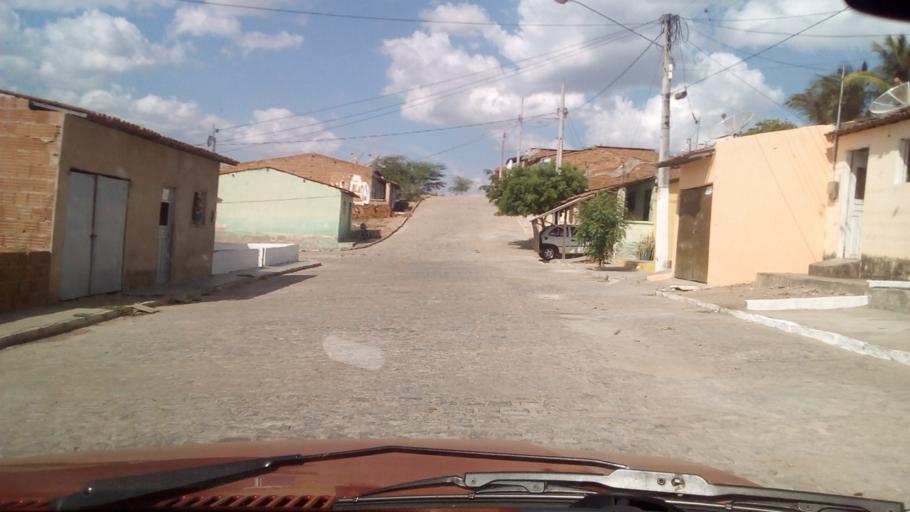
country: BR
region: Paraiba
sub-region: Arara
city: Arara
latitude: -6.8254
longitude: -35.7620
